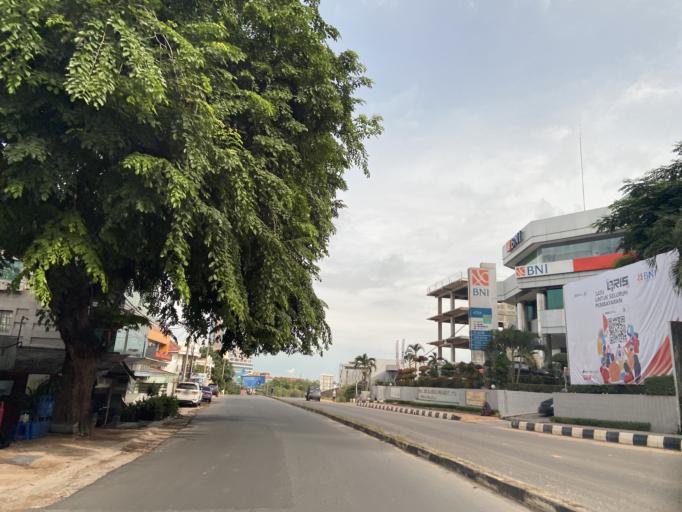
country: SG
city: Singapore
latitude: 1.1430
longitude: 104.0146
